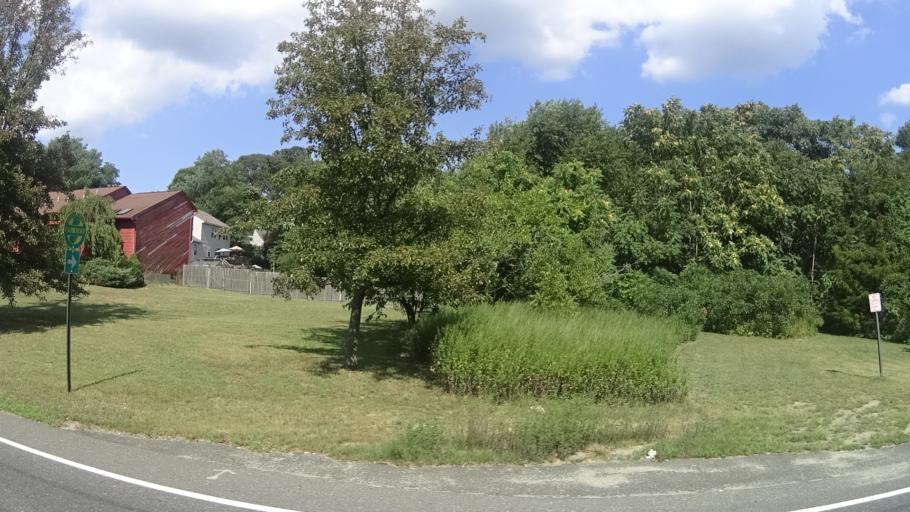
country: US
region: New Jersey
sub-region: Monmouth County
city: Ramtown
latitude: 40.1469
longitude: -74.1045
